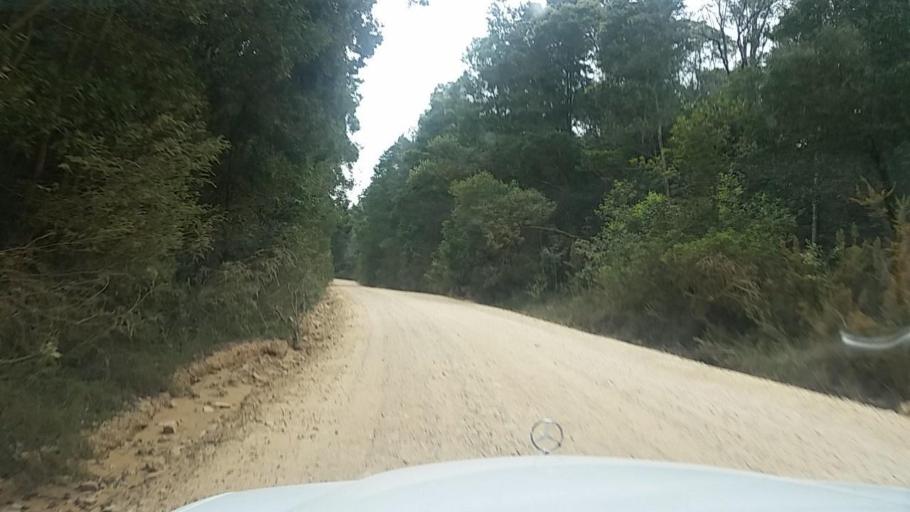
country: ZA
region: Western Cape
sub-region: Eden District Municipality
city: Knysna
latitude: -33.9967
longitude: 23.1218
